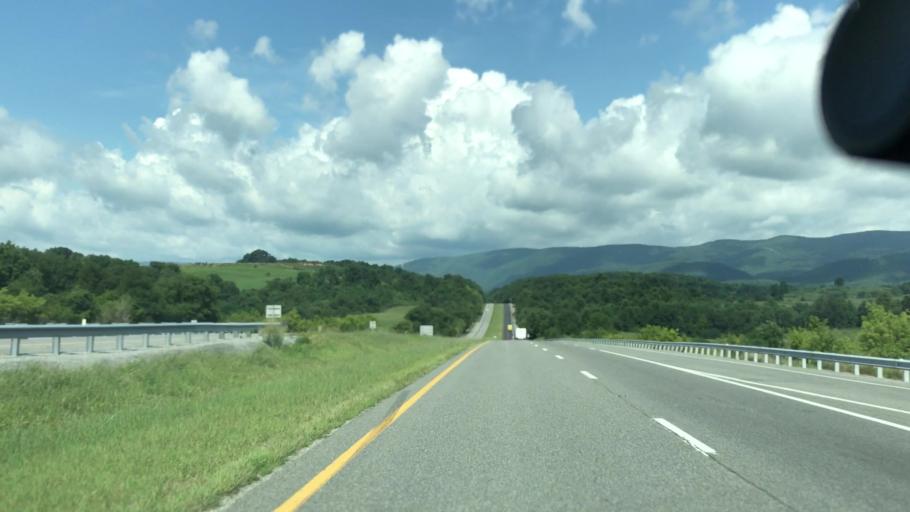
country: US
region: Virginia
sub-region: Giles County
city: Pearisburg
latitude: 37.3329
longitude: -80.6949
